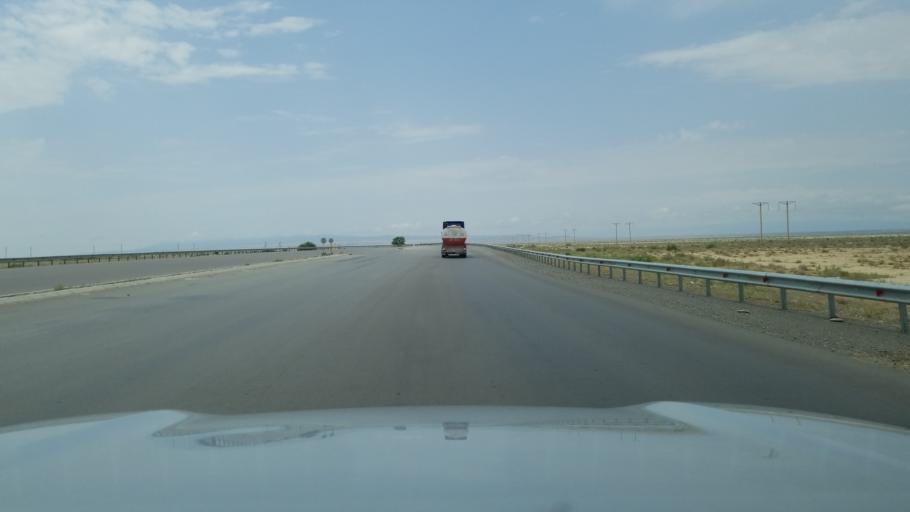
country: TM
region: Balkan
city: Gazanjyk
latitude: 39.2625
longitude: 55.3059
